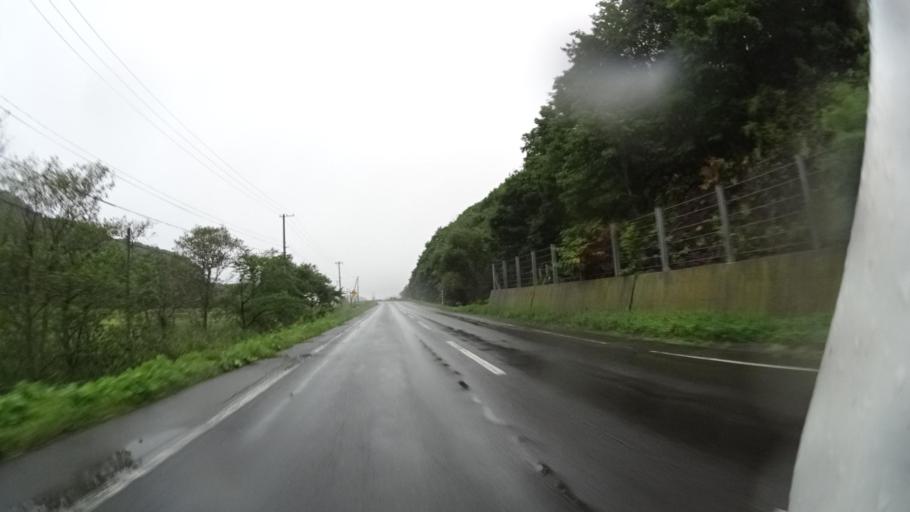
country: JP
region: Hokkaido
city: Kushiro
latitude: 43.0785
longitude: 144.8408
